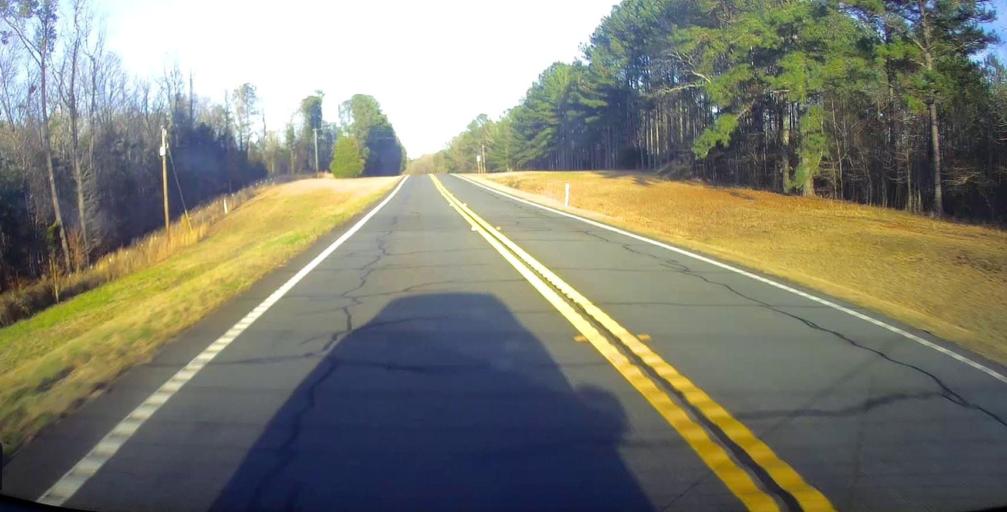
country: US
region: Georgia
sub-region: Talbot County
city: Talbotton
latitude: 32.7881
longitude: -84.5138
